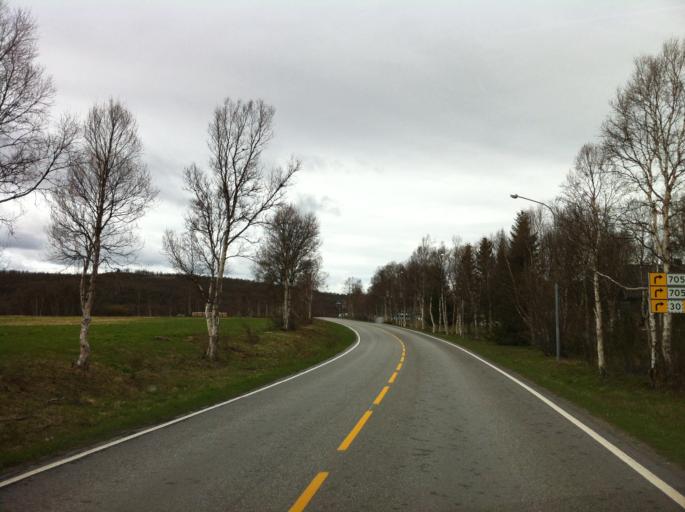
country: NO
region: Sor-Trondelag
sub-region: Tydal
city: Aas
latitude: 62.6458
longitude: 11.8780
